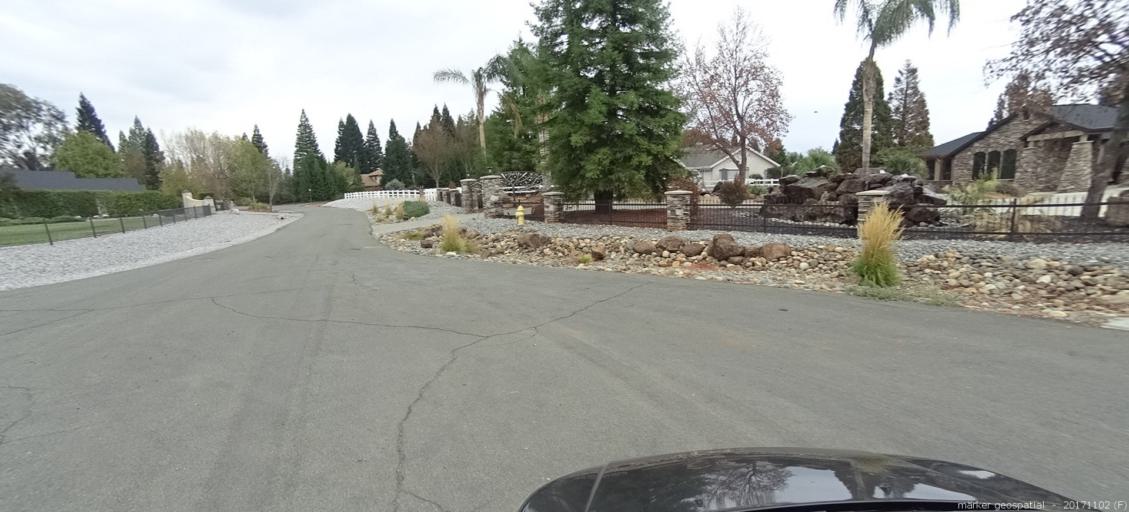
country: US
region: California
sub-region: Shasta County
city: Shasta Lake
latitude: 40.6518
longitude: -122.3231
